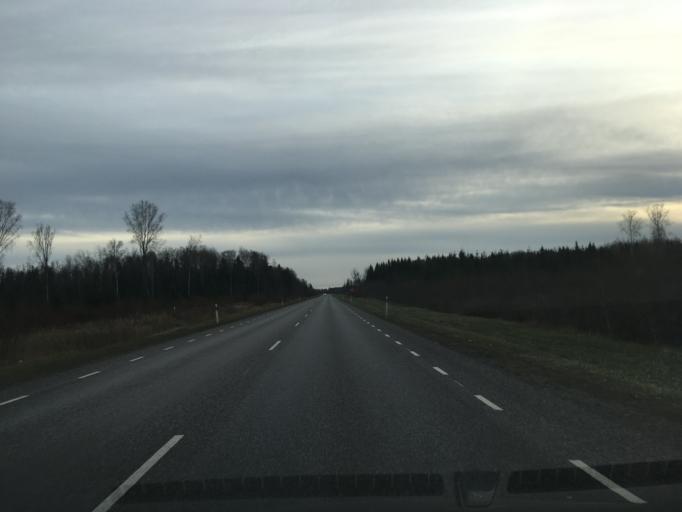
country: EE
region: Ida-Virumaa
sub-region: Johvi vald
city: Johvi
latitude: 59.3503
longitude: 27.4675
